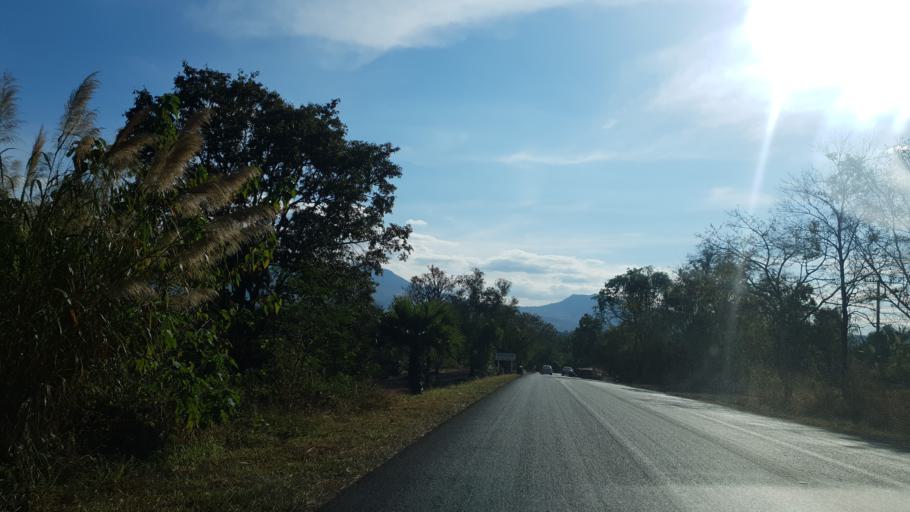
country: TH
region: Loei
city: Phu Ruea
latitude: 17.4461
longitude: 101.4760
